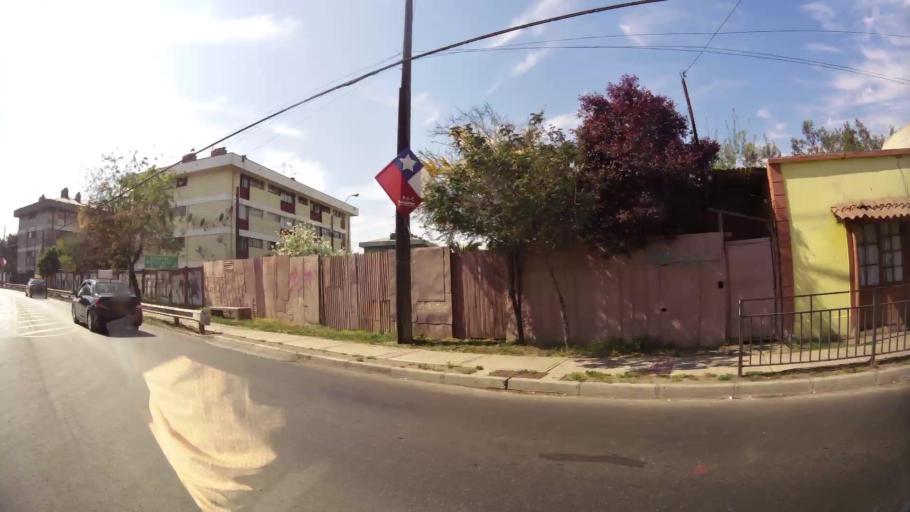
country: CL
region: Santiago Metropolitan
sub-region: Provincia de Talagante
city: Talagante
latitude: -33.6691
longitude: -70.9382
